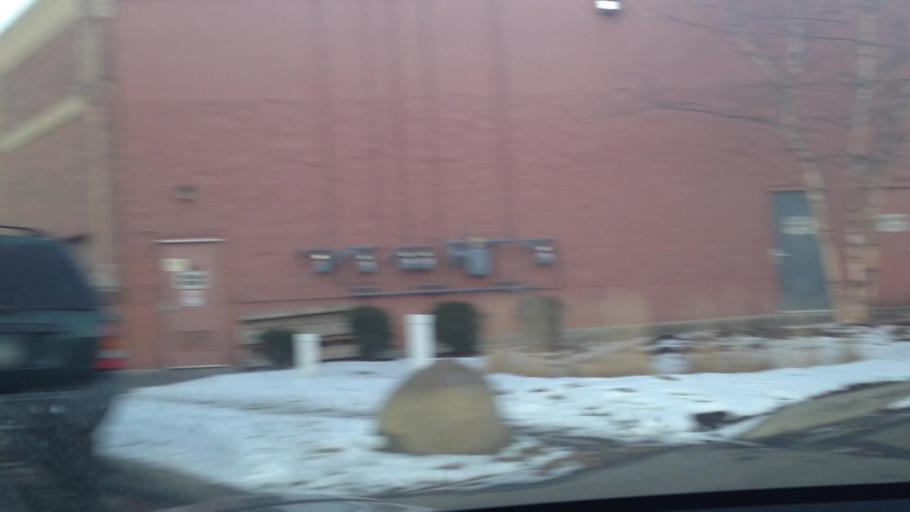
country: US
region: Minnesota
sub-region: Hennepin County
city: Saint Louis Park
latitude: 44.9468
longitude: -93.3227
